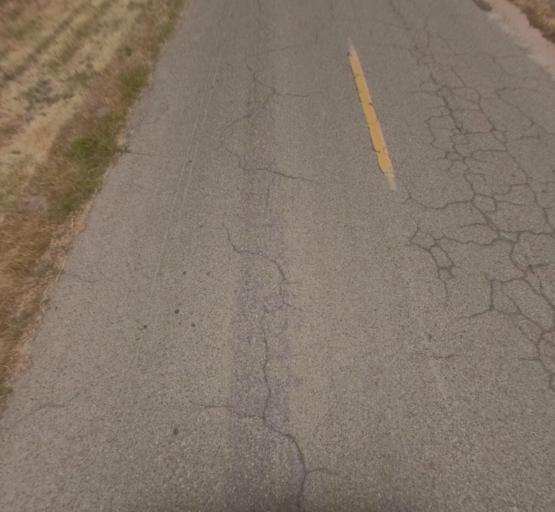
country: US
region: California
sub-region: Madera County
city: Parkwood
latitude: 36.8781
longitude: -120.1649
